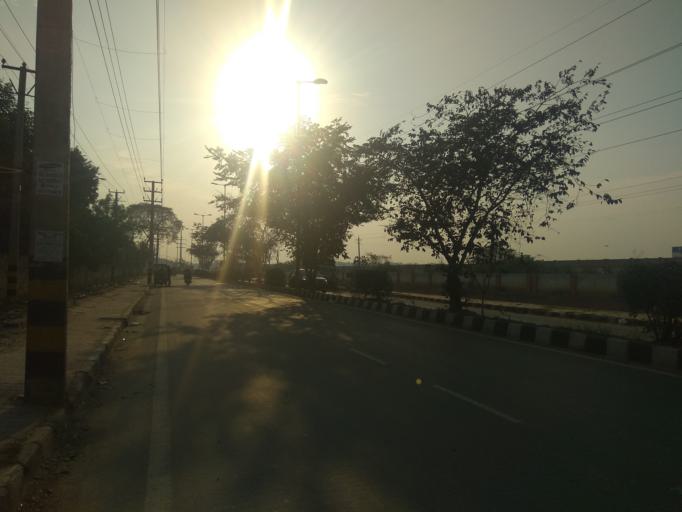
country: IN
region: NCT
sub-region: West Delhi
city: Nangloi Jat
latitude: 28.6432
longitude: 77.0666
